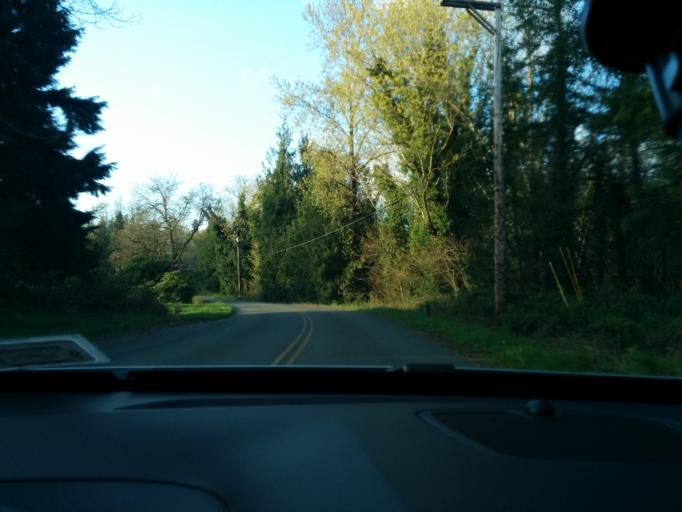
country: US
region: Washington
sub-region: Snohomish County
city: Gold Bar
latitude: 47.8715
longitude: -121.7315
